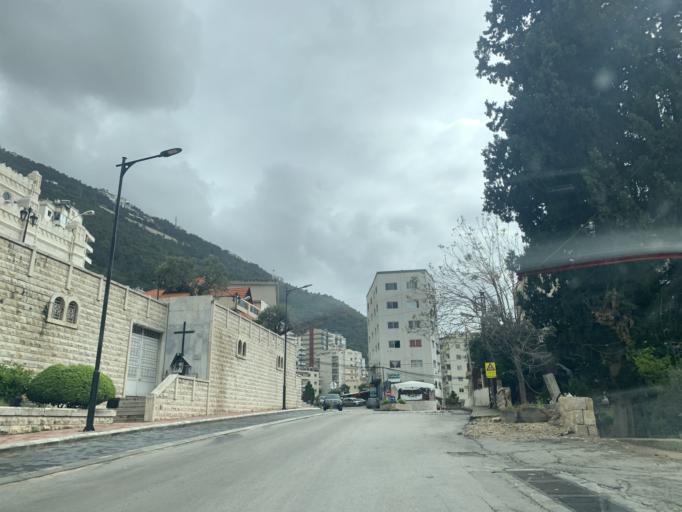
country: LB
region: Mont-Liban
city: Djounie
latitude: 33.9877
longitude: 35.6436
